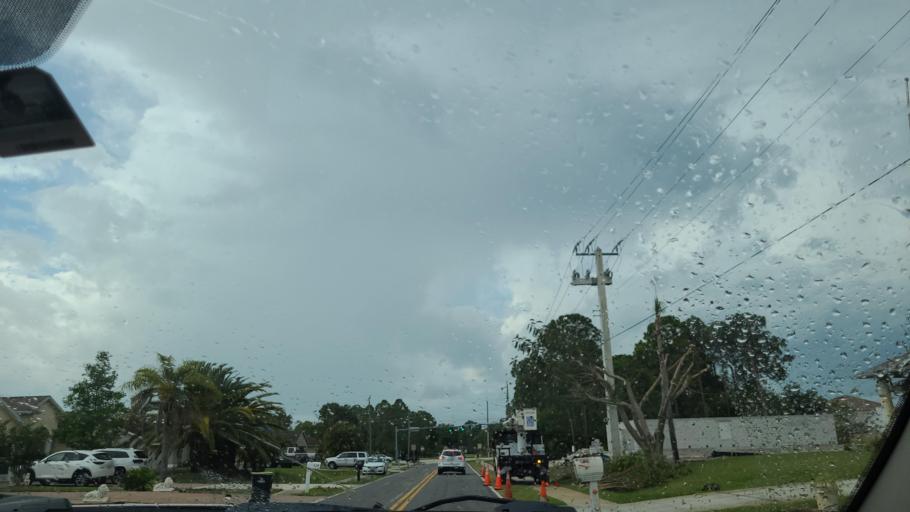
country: US
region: Florida
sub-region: Brevard County
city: Grant-Valkaria
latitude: 27.9566
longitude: -80.6470
